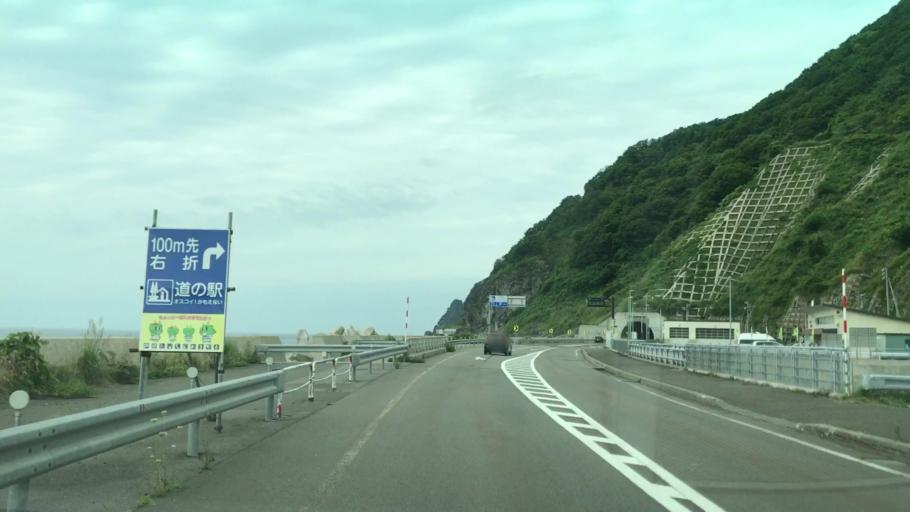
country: JP
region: Hokkaido
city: Iwanai
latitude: 43.1644
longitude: 140.3861
